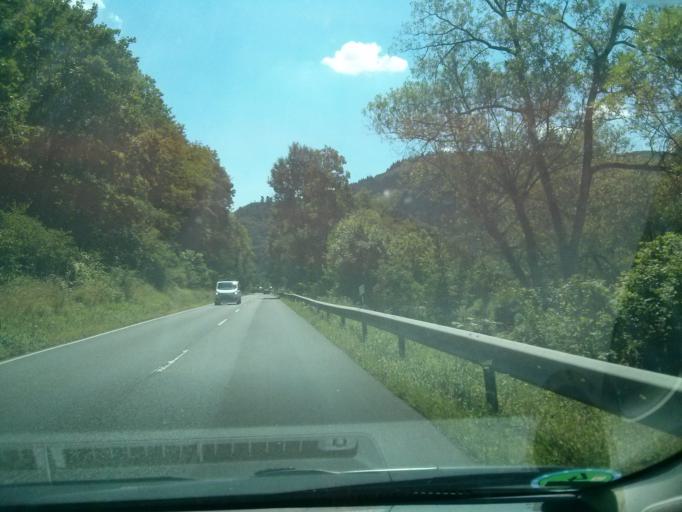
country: DE
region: Rheinland-Pfalz
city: Altenahr
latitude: 50.5047
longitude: 6.9807
